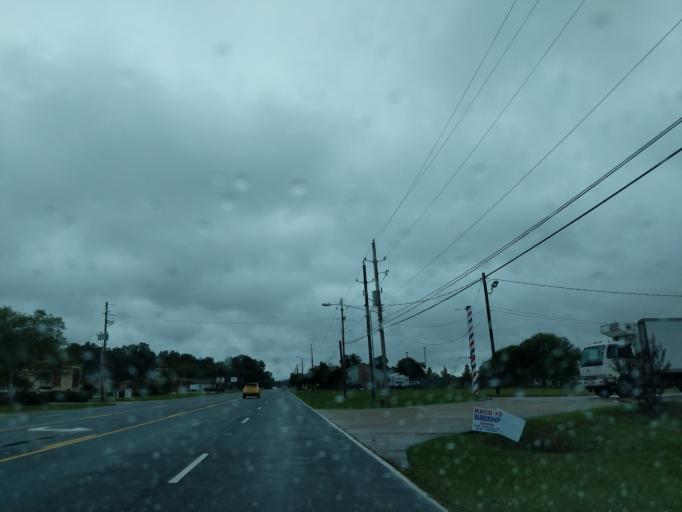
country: US
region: Louisiana
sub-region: Bossier Parish
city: Bossier City
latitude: 32.5136
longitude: -93.6850
